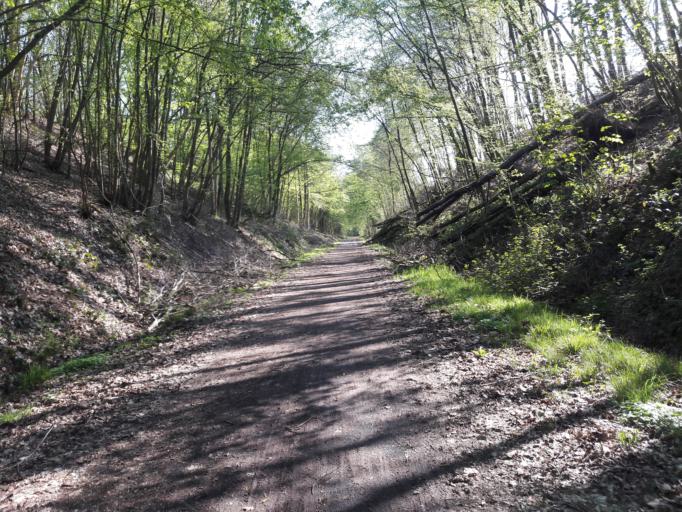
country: FR
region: Nord-Pas-de-Calais
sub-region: Departement du Nord
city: Sains-du-Nord
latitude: 50.1422
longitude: 4.0676
